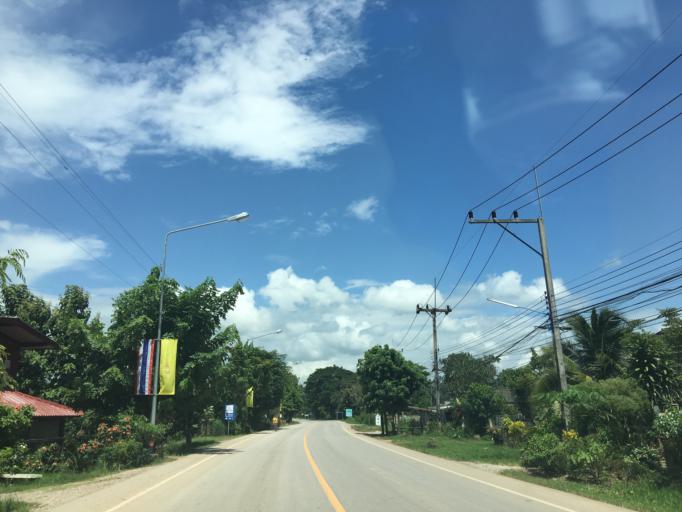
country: TH
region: Chiang Rai
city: Pa Daet
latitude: 19.4976
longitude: 99.9712
